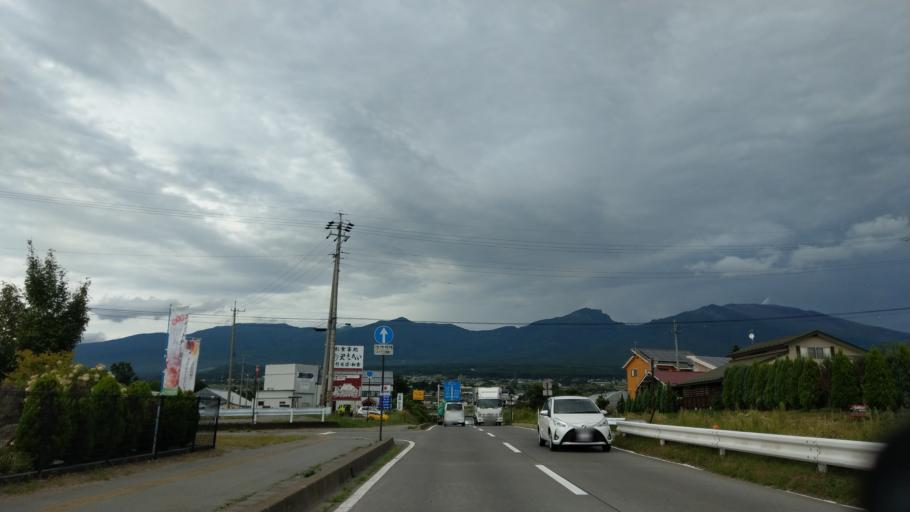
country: JP
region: Nagano
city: Komoro
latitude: 36.3100
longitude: 138.4565
